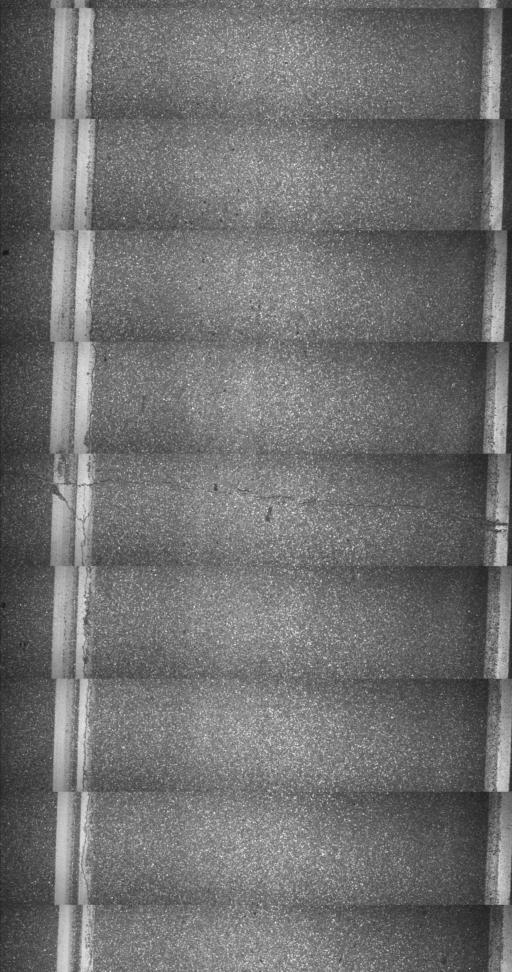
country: US
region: Vermont
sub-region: Washington County
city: Barre
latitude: 44.2558
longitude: -72.2702
